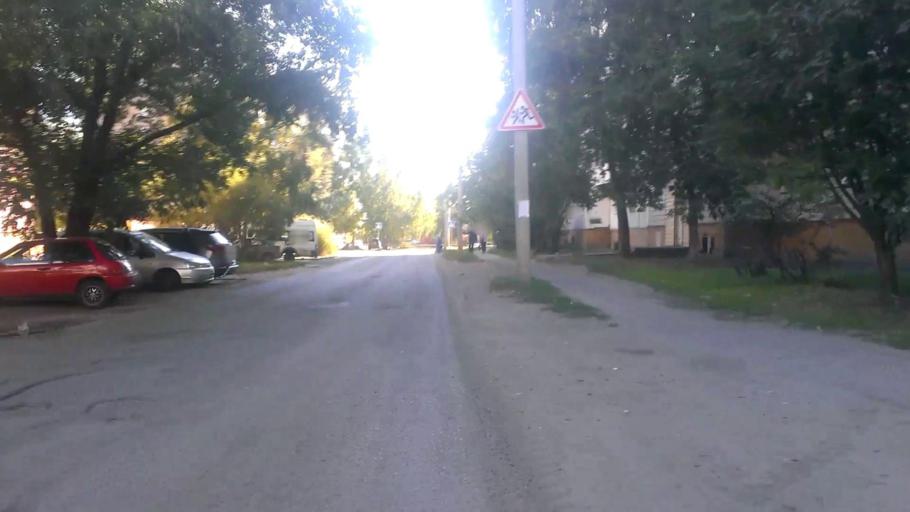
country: RU
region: Altai Krai
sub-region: Gorod Barnaulskiy
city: Barnaul
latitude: 53.3733
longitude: 83.6913
